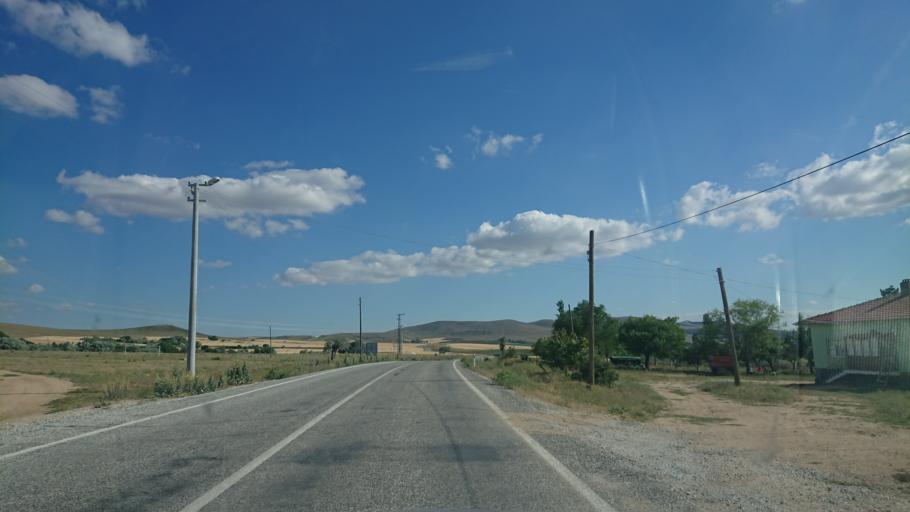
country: TR
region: Aksaray
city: Agacoren
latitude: 38.7799
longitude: 33.9332
